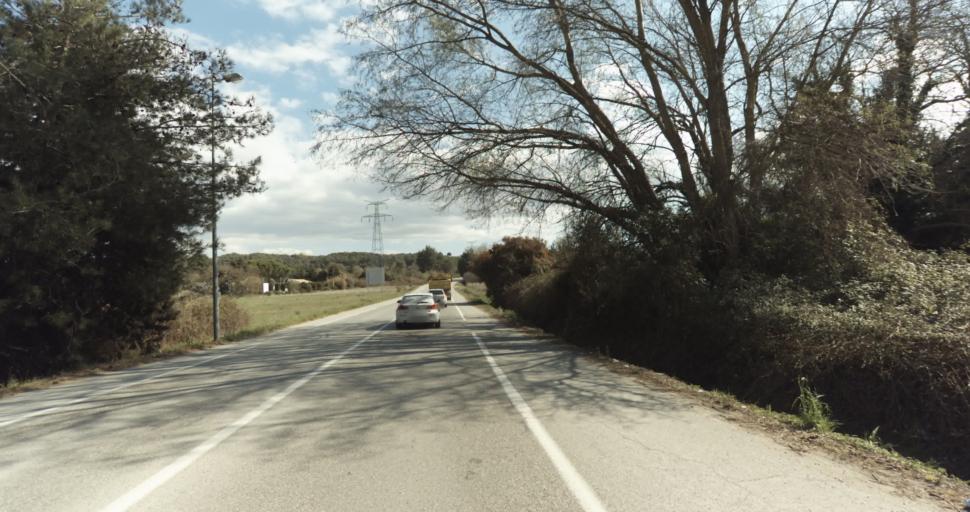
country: FR
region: Provence-Alpes-Cote d'Azur
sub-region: Departement des Bouches-du-Rhone
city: Gardanne
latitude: 43.4637
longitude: 5.4862
